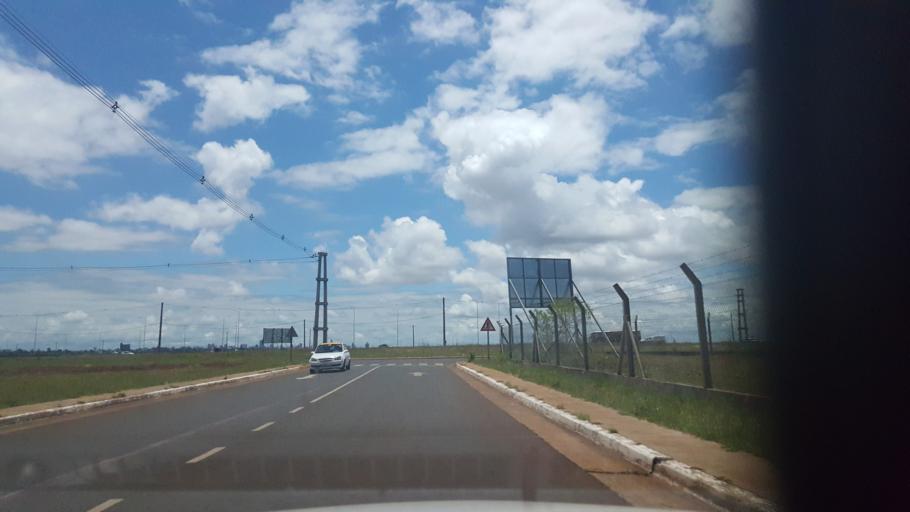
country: AR
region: Misiones
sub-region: Departamento de Capital
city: Posadas
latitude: -27.4169
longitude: -55.8859
